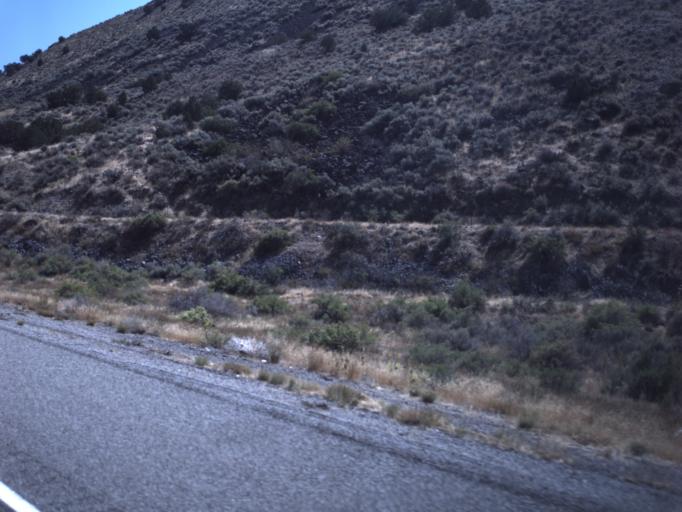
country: US
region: Utah
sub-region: Sevier County
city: Salina
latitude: 38.9302
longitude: -111.8287
